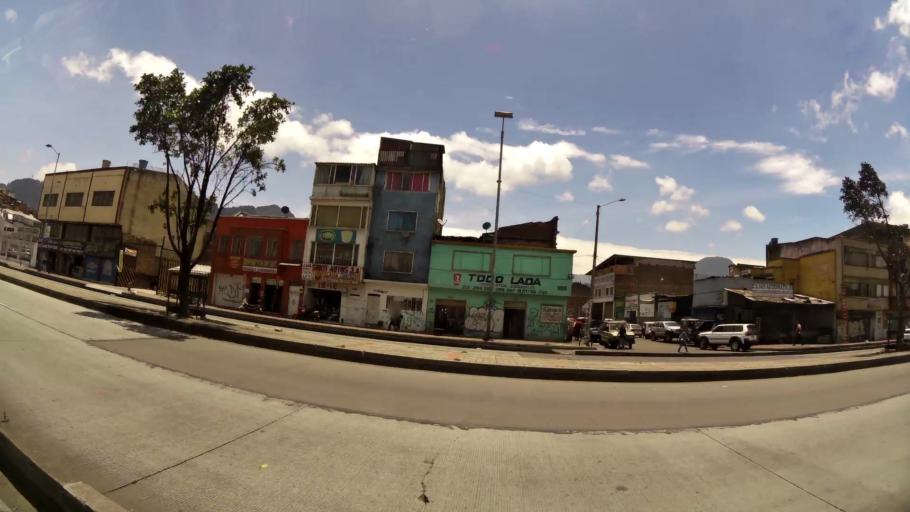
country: CO
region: Bogota D.C.
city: Bogota
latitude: 4.5927
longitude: -74.0883
